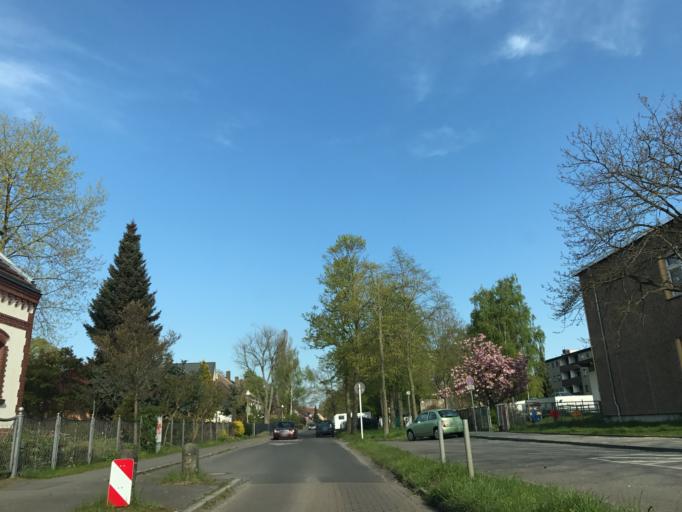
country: DE
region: Berlin
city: Wilhelmstadt
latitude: 52.5129
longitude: 13.1668
